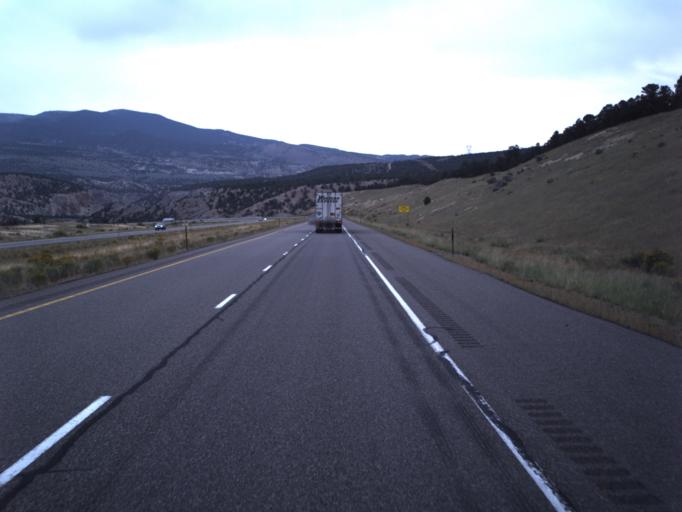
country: US
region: Utah
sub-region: Sevier County
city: Monroe
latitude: 38.5493
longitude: -112.3699
